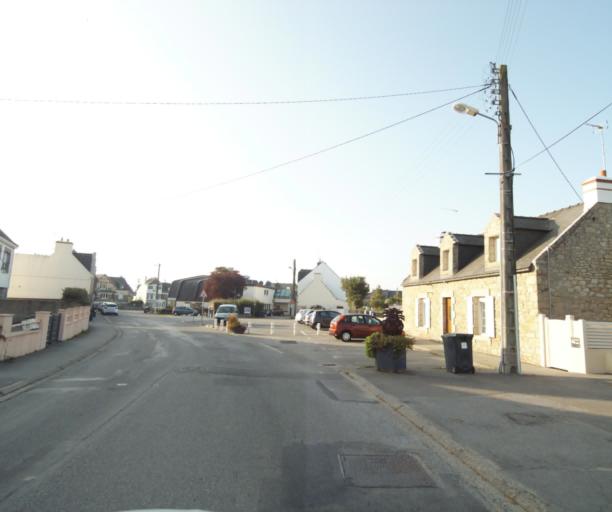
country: FR
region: Brittany
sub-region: Departement du Morbihan
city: Riantec
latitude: 47.7126
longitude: -3.3107
